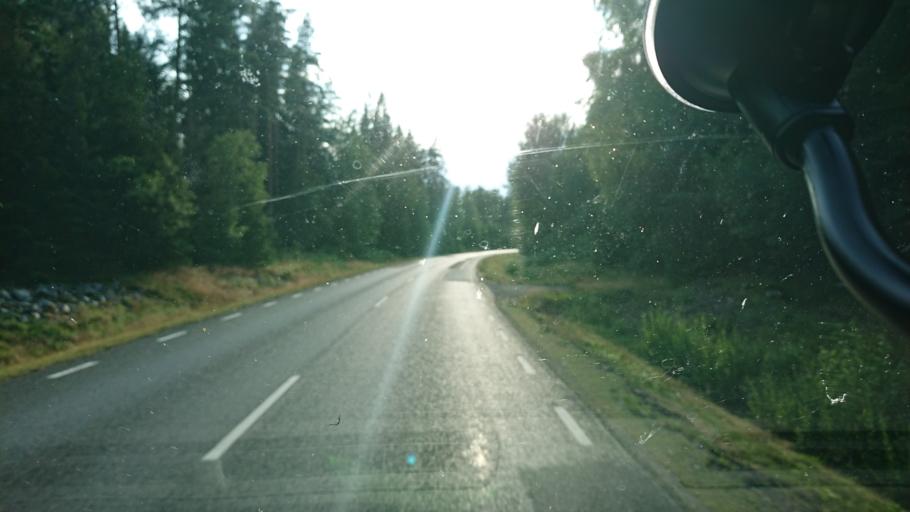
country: SE
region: Kronoberg
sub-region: Vaxjo Kommun
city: Braas
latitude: 57.0224
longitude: 15.0125
